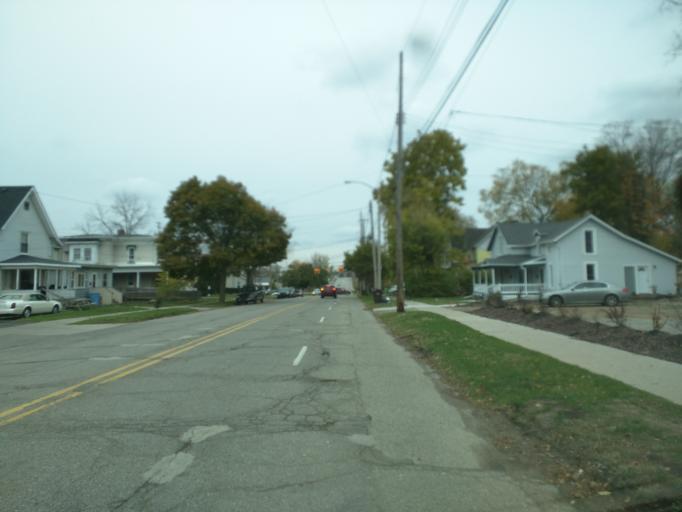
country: US
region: Michigan
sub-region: Ingham County
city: Lansing
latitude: 42.7476
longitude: -84.5553
